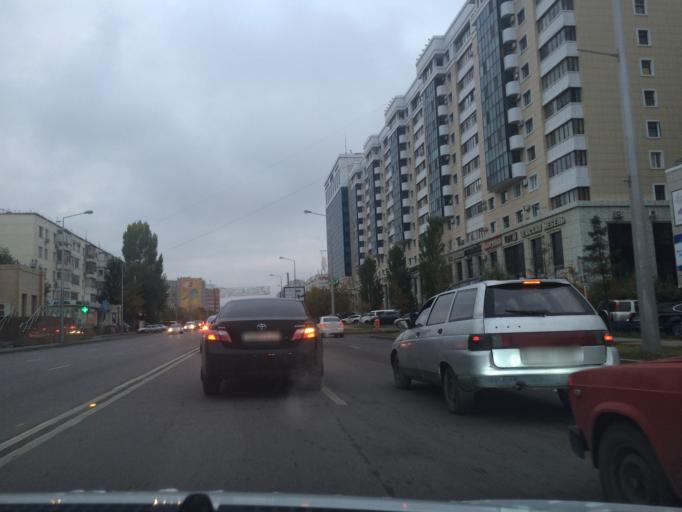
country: KZ
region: Astana Qalasy
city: Astana
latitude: 51.1686
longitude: 71.4081
